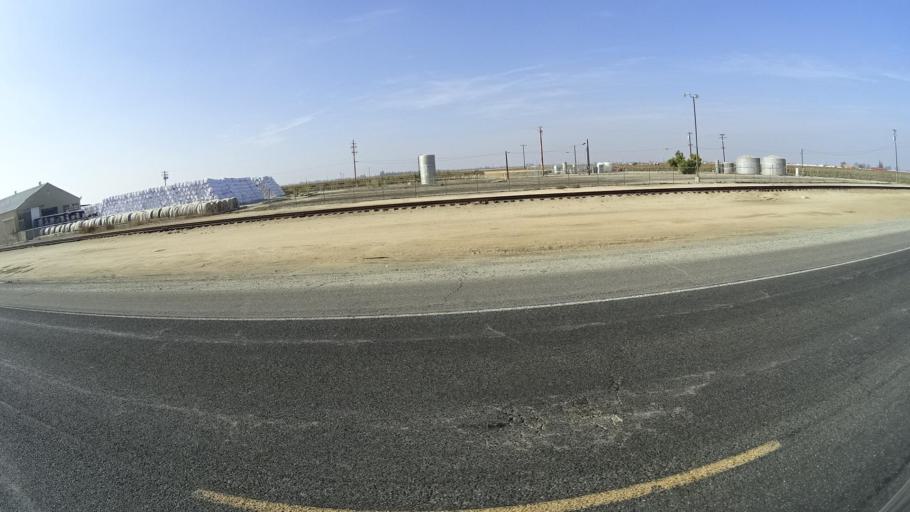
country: US
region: California
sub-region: Kern County
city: McFarland
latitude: 35.6681
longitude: -119.1901
